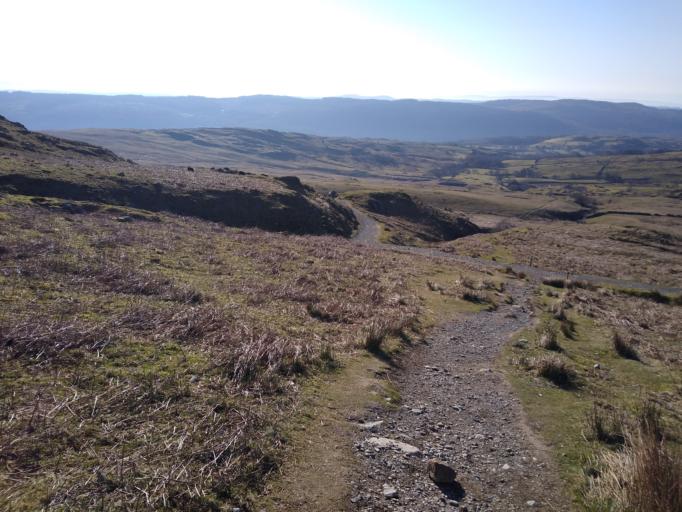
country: GB
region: England
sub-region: Cumbria
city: Ulverston
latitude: 54.3588
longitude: -3.1191
